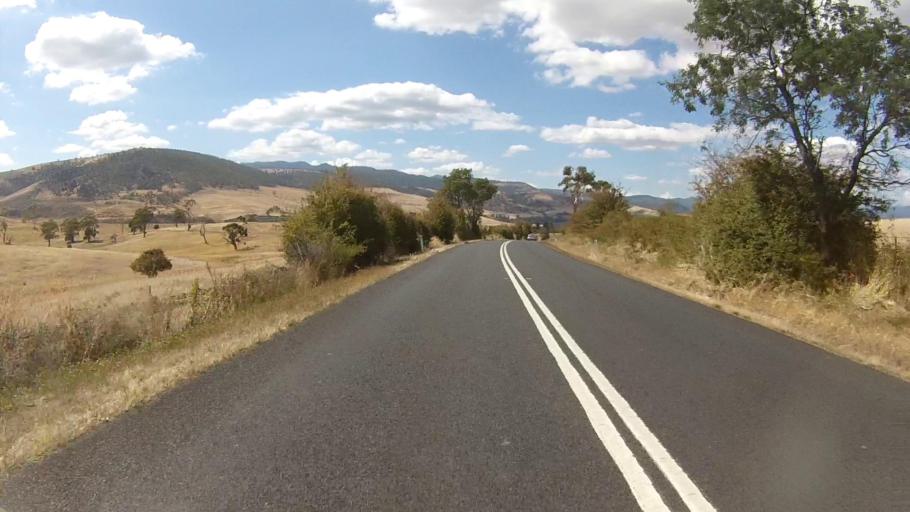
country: AU
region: Tasmania
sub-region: Derwent Valley
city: New Norfolk
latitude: -42.7358
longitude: 146.9392
